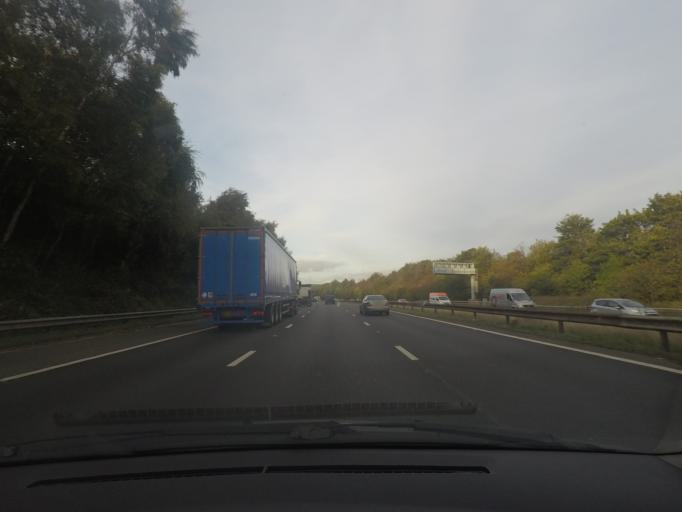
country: GB
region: England
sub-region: Barnsley
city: Darton
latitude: 53.5805
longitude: -1.5372
